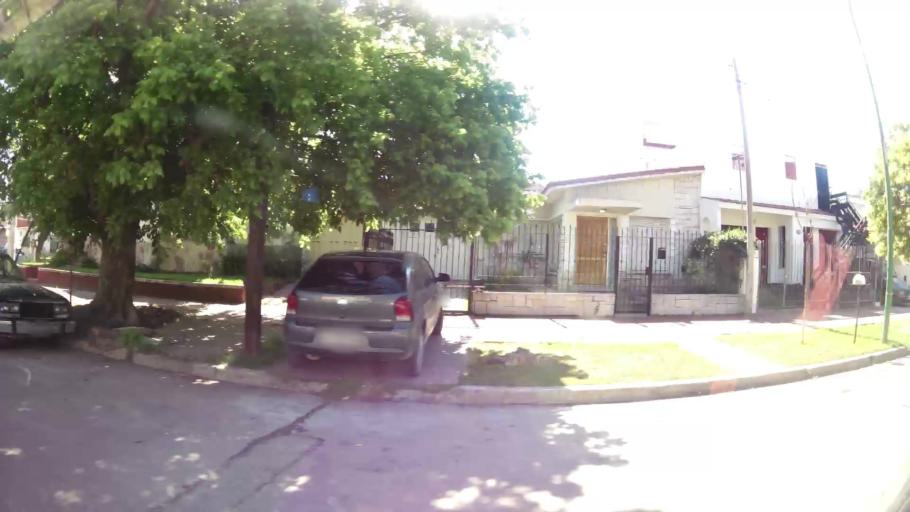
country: AR
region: Cordoba
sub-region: Departamento de Capital
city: Cordoba
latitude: -31.4204
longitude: -64.1595
